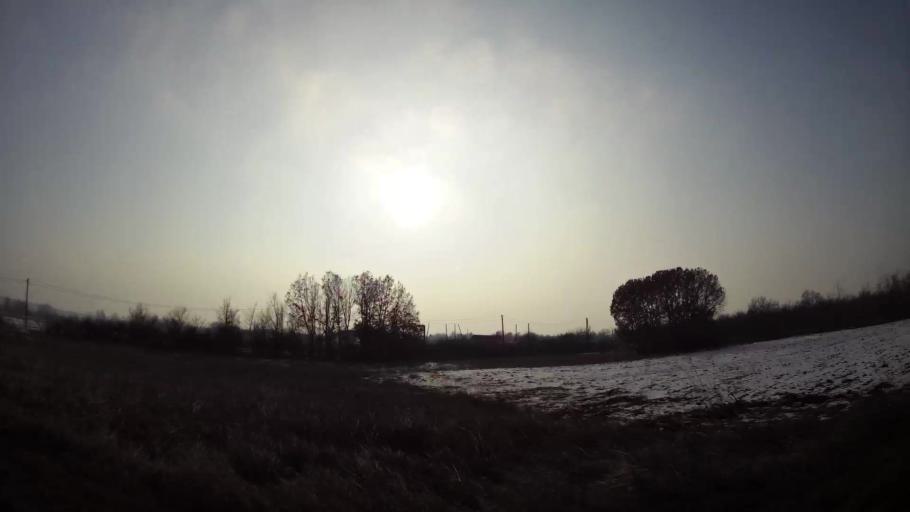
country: MK
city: Miladinovci
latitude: 41.9732
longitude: 21.6330
